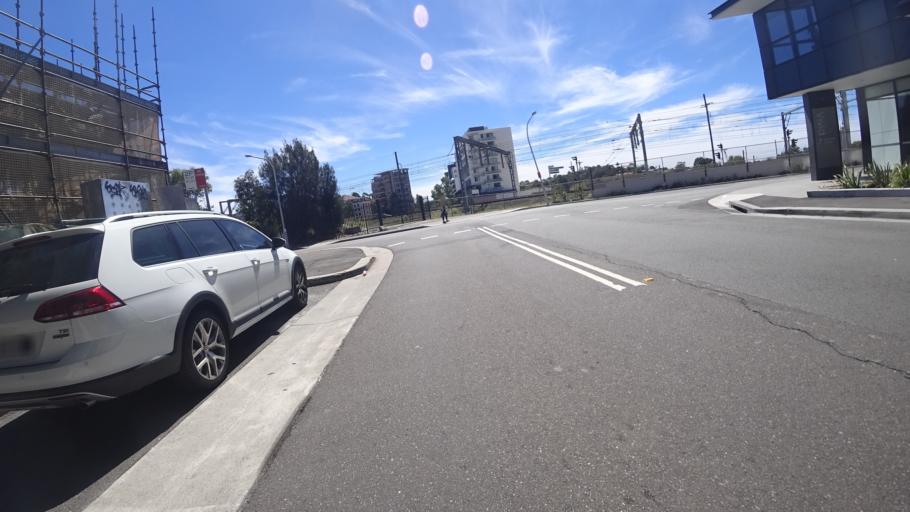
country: AU
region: New South Wales
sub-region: Rockdale
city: Arncliffe
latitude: -33.9298
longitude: 151.1527
